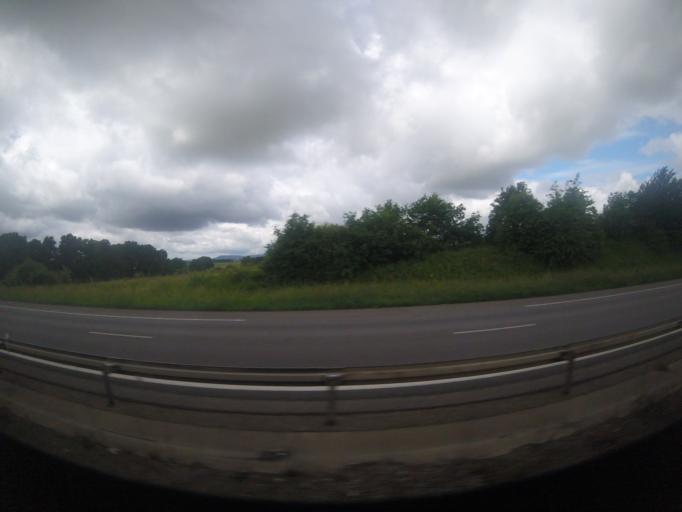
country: FR
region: Lorraine
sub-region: Departement de la Moselle
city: Argancy
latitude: 49.1741
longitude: 6.2504
